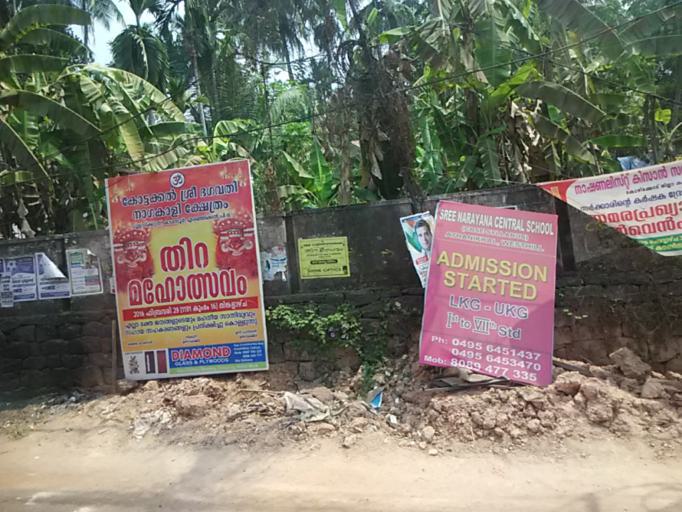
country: IN
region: Kerala
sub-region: Kozhikode
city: Kozhikode
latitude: 11.3261
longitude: 75.7652
